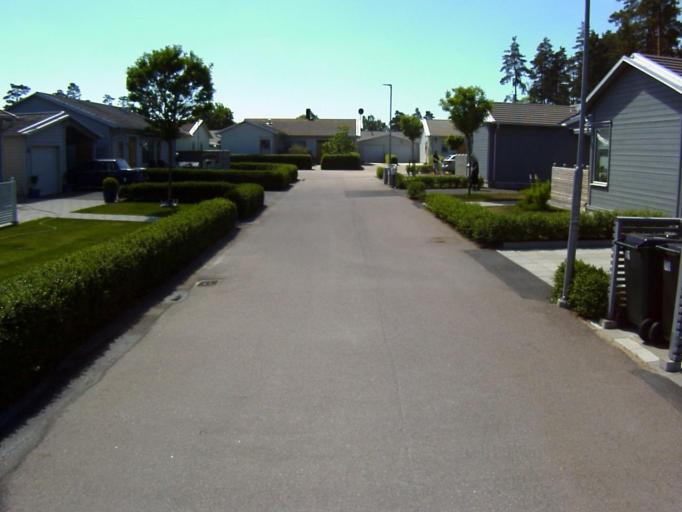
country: SE
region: Skane
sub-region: Kristianstads Kommun
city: Ahus
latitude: 55.9397
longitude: 14.2917
